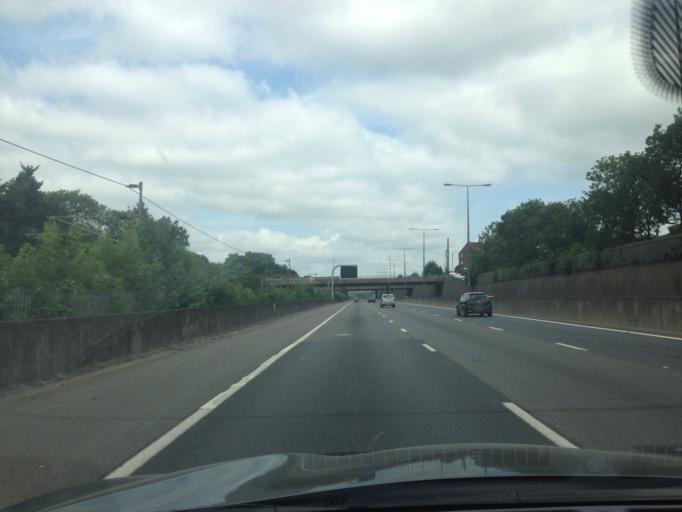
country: GB
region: England
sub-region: Greater London
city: Edgware
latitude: 51.6187
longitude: -0.2542
